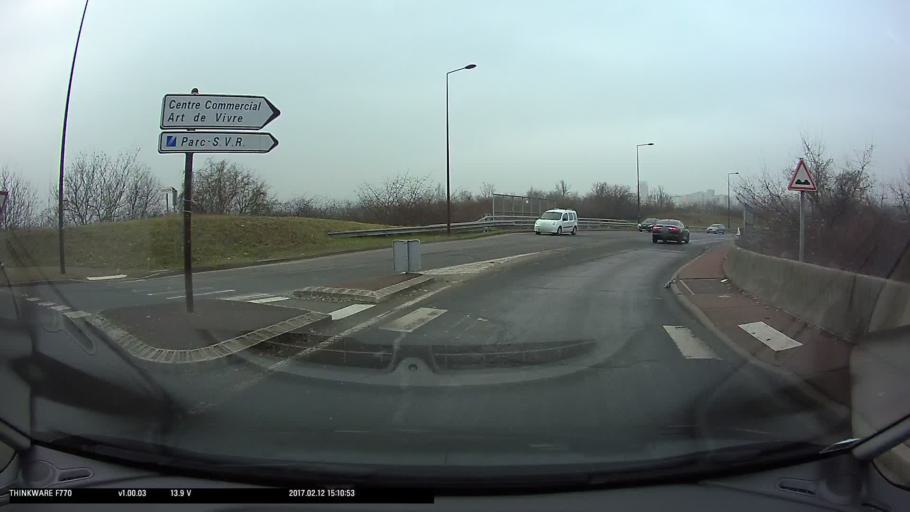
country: FR
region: Ile-de-France
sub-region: Departement du Val-d'Oise
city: Eragny
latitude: 49.0280
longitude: 2.1022
